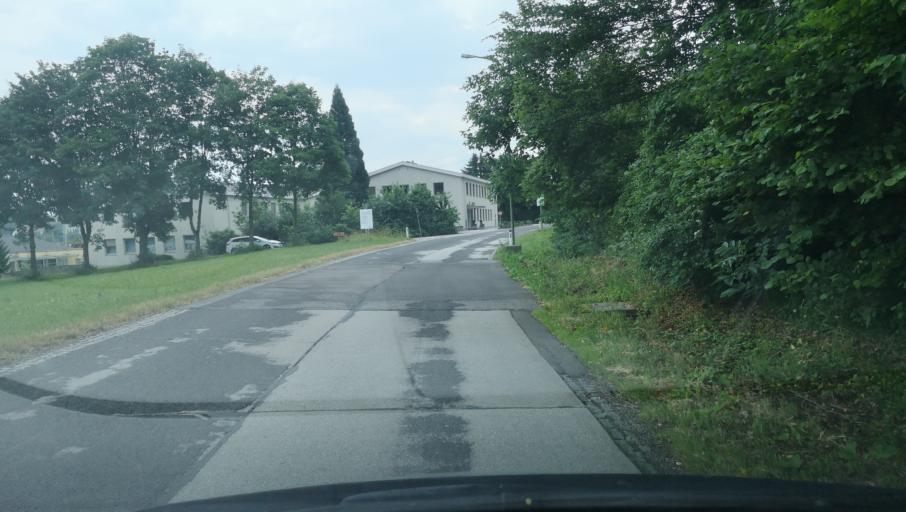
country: AT
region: Lower Austria
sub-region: Politischer Bezirk Melk
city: Ybbs an der Donau
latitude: 48.1896
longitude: 15.0630
